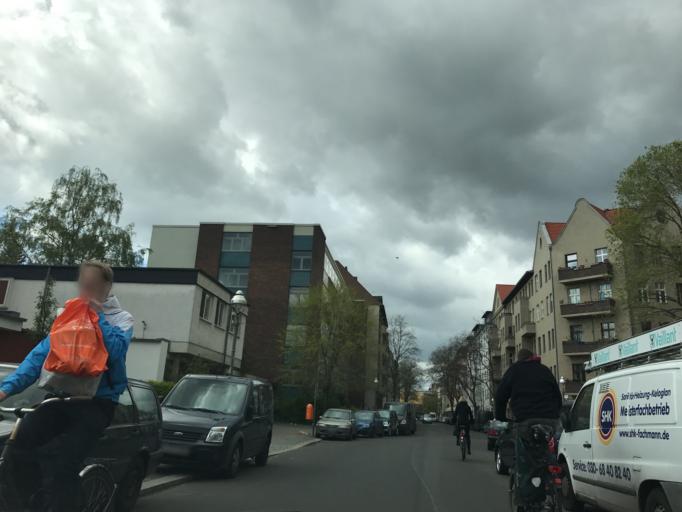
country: DE
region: Berlin
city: Berlin Treptow
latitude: 52.4776
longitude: 13.4436
